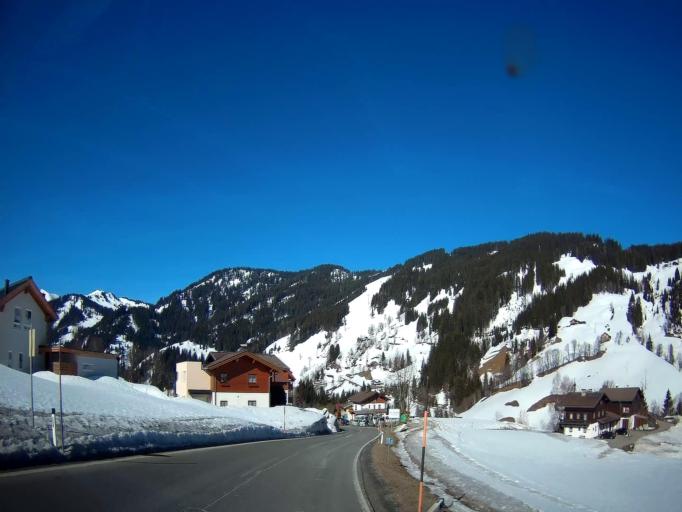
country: AT
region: Salzburg
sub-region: Politischer Bezirk Zell am See
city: Dienten am Hochkonig
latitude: 47.3860
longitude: 13.0140
